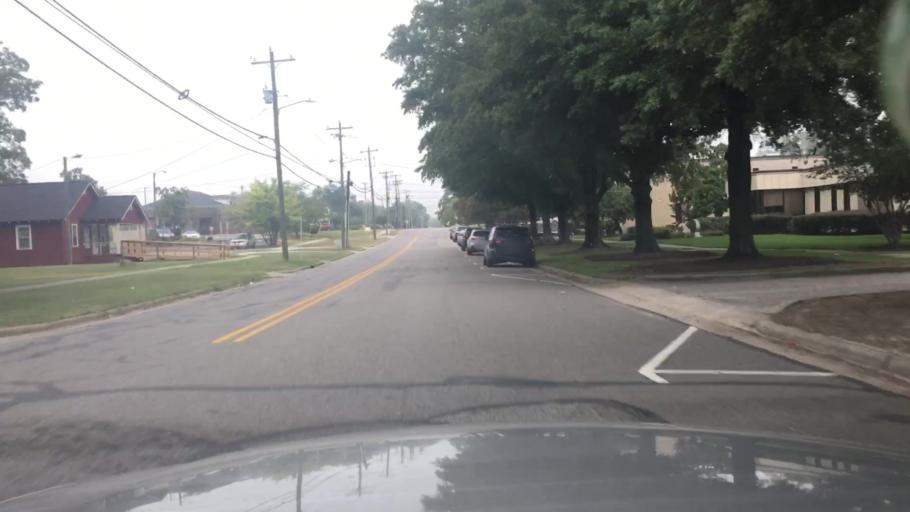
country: US
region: North Carolina
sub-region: Cumberland County
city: Fayetteville
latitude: 35.0588
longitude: -78.8747
